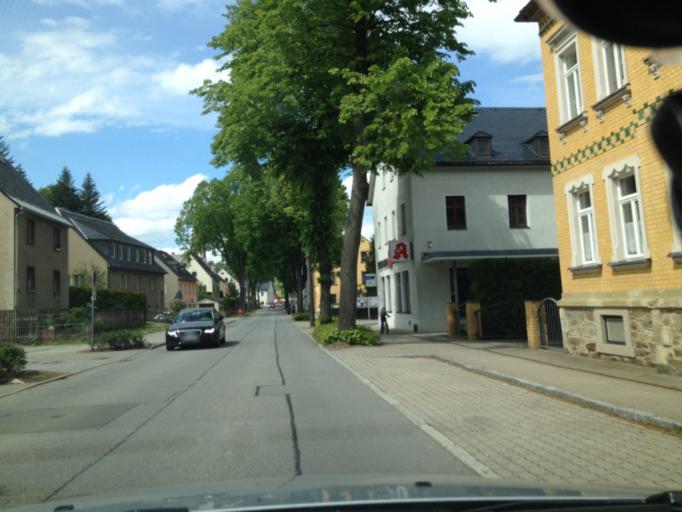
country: DE
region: Saxony
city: Annaberg-Buchholz
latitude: 50.5357
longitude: 12.9952
